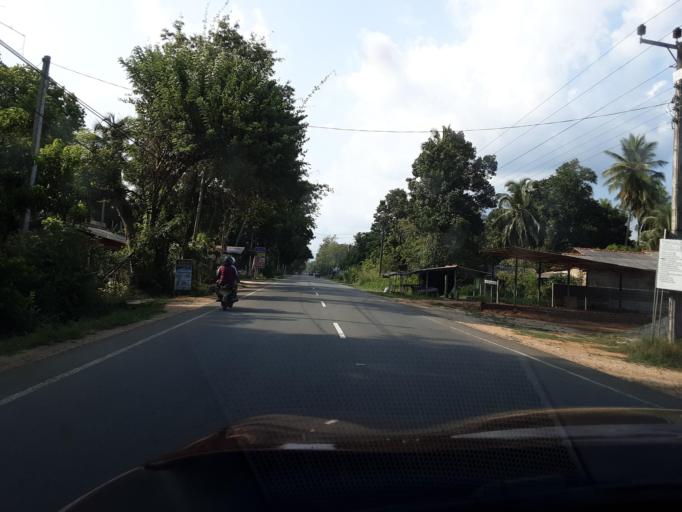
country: LK
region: Uva
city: Haputale
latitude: 6.6626
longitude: 81.1142
